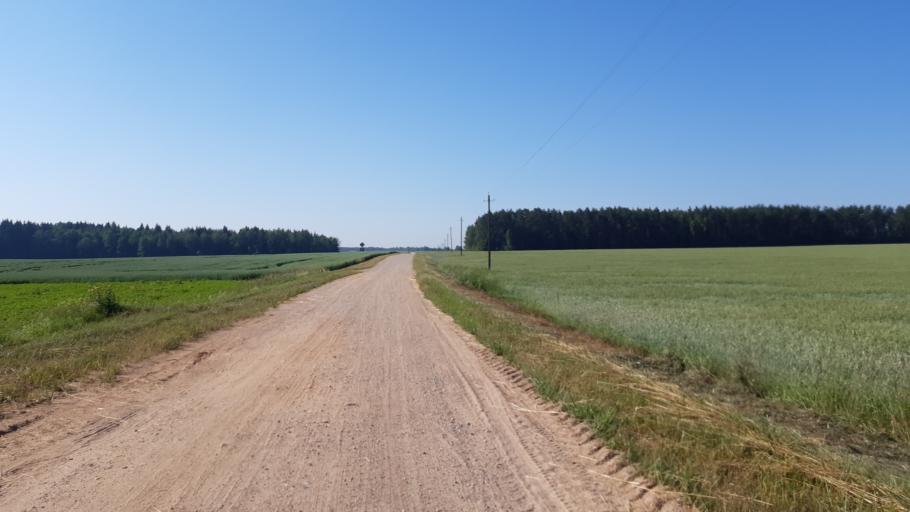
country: BY
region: Minsk
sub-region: Smalyavitski Rayon
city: Oktjabr'skij
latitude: 54.0948
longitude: 28.2010
